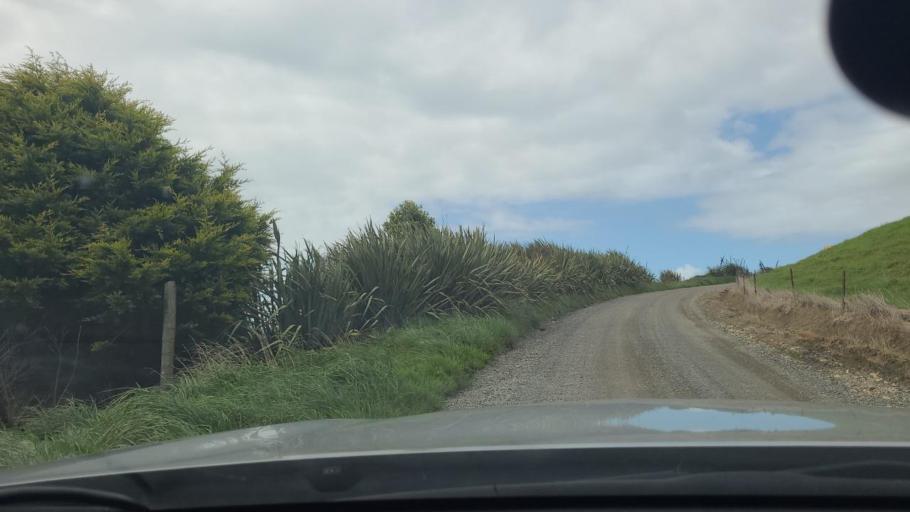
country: NZ
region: Southland
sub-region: Southland District
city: Riverton
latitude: -46.3671
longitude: 168.0041
